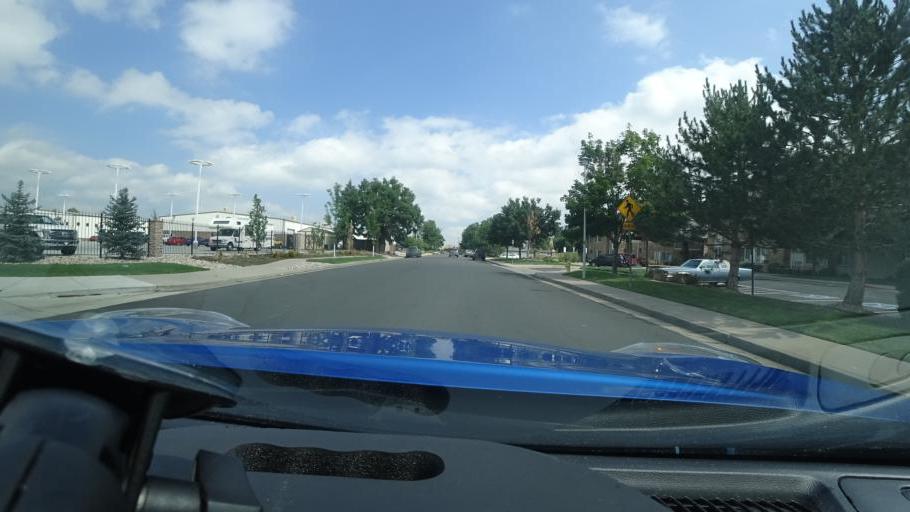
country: US
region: Colorado
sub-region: Adams County
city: Aurora
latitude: 39.7123
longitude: -104.8637
